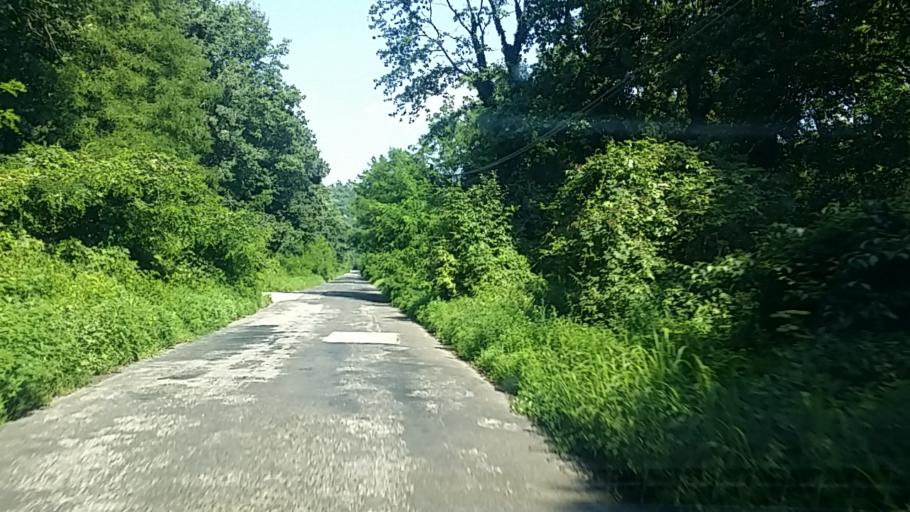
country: HU
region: Zala
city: Lenti
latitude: 46.5541
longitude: 16.5834
